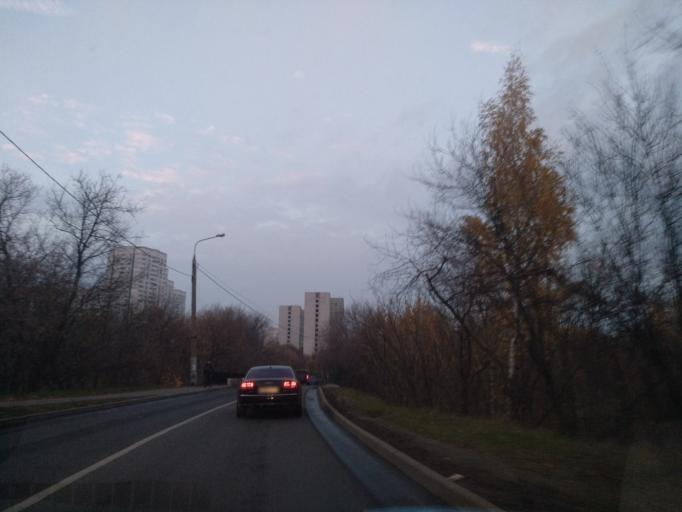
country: RU
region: Moscow
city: Leonovo
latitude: 55.8647
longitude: 37.6419
